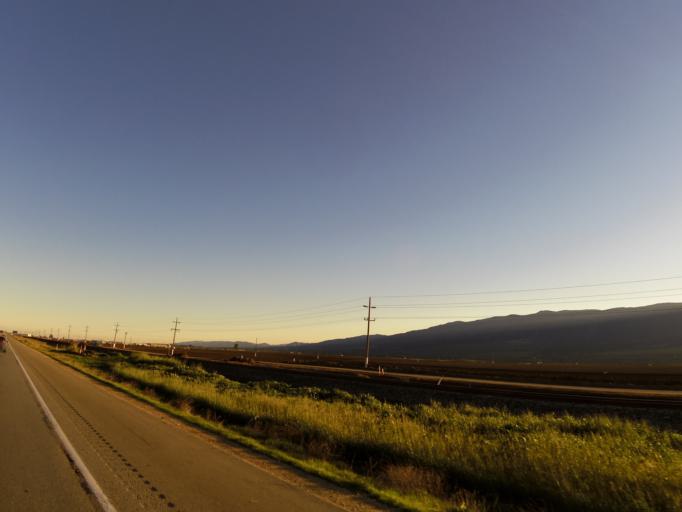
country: US
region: California
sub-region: Monterey County
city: Gonzales
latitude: 36.4784
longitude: -121.4099
